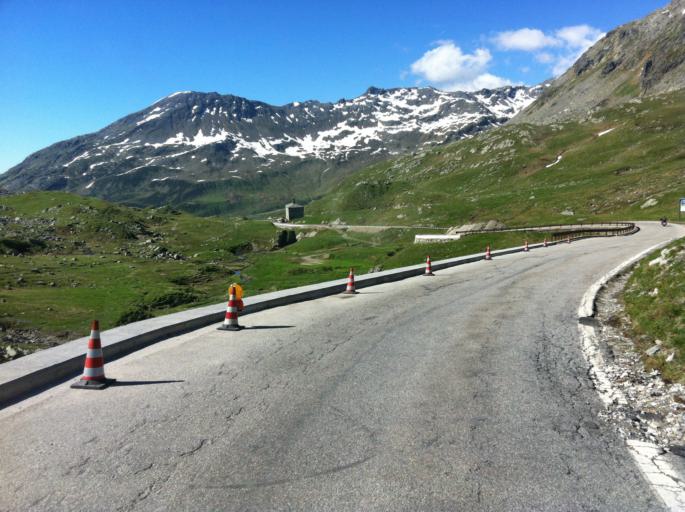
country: IT
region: Lombardy
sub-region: Provincia di Sondrio
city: Campodolcino
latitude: 46.5044
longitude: 9.3310
